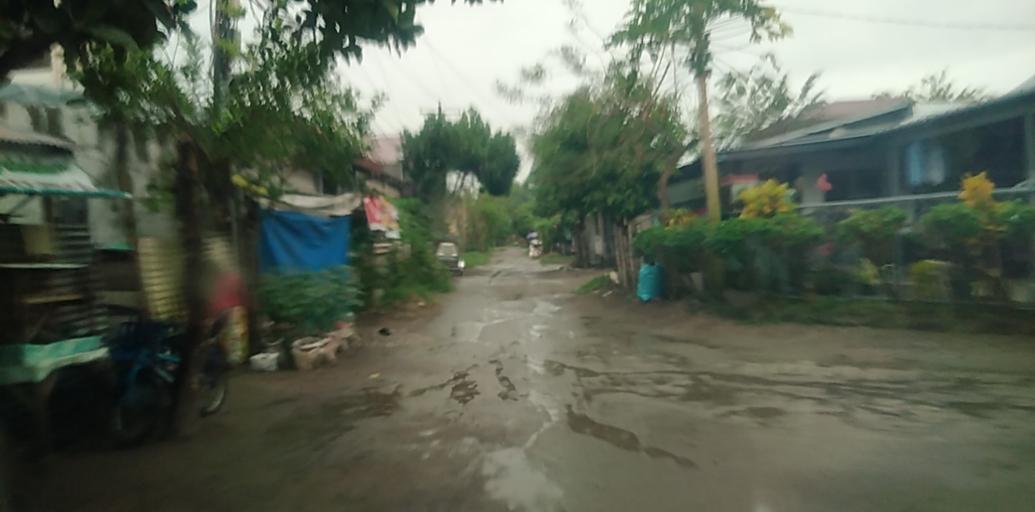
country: PH
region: Central Luzon
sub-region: Province of Pampanga
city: Arenas
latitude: 15.1726
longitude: 120.6830
